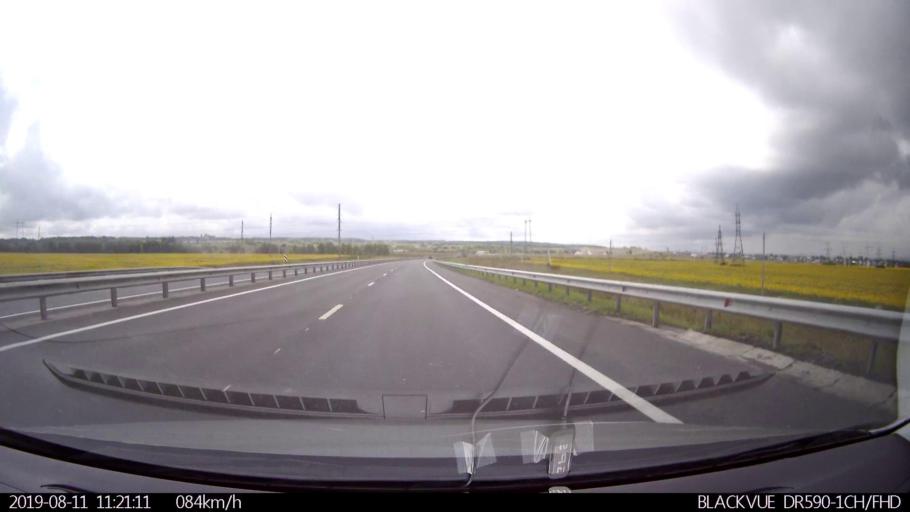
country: RU
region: Ulyanovsk
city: Novoul'yanovsk
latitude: 54.1490
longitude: 48.2642
